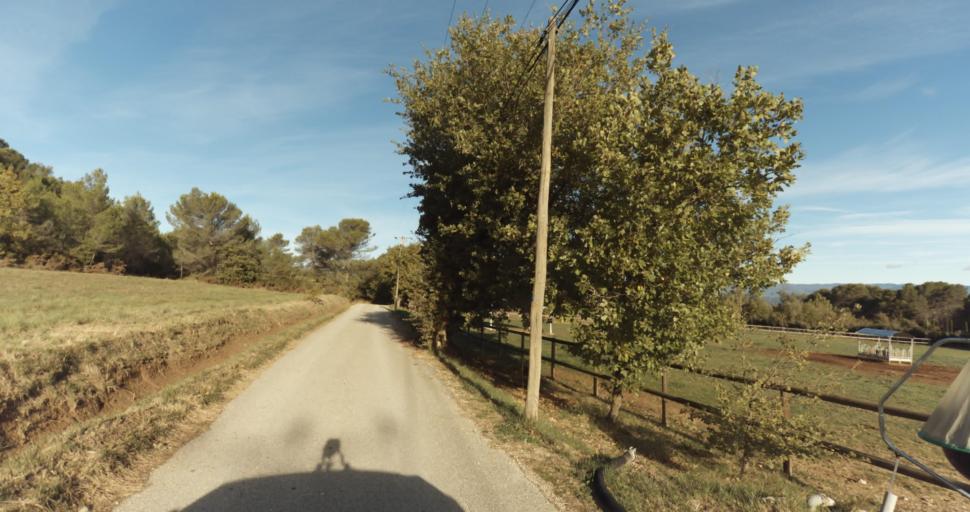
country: FR
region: Provence-Alpes-Cote d'Azur
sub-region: Departement des Bouches-du-Rhone
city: Venelles
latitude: 43.6175
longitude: 5.4758
